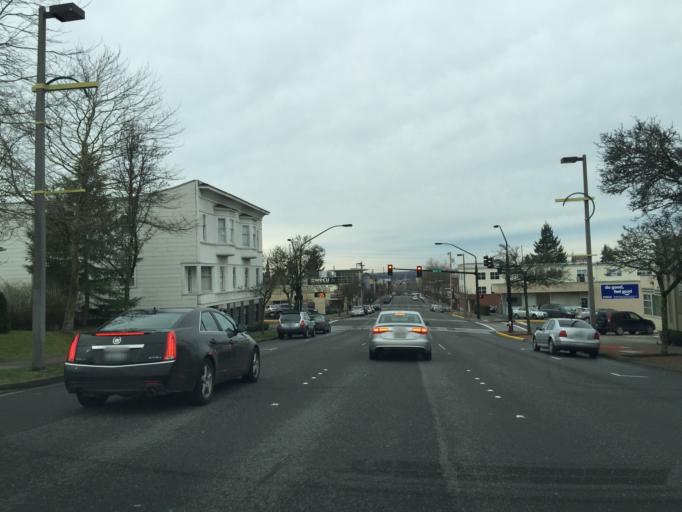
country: US
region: Washington
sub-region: Whatcom County
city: Bellingham
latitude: 48.7454
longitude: -122.4724
